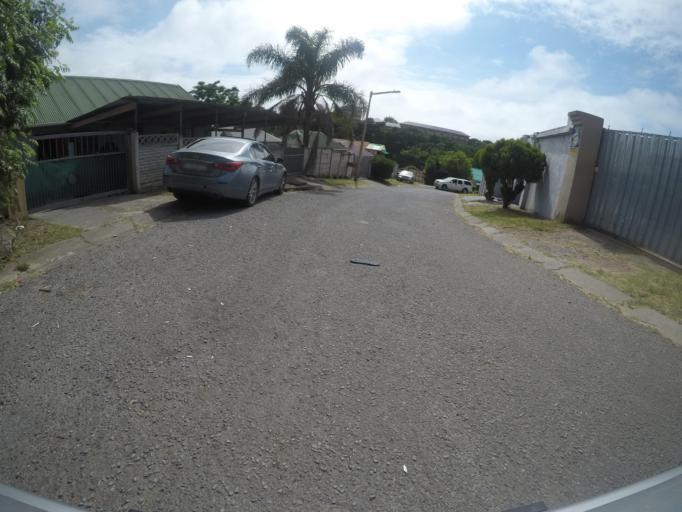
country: ZA
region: Eastern Cape
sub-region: Buffalo City Metropolitan Municipality
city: East London
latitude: -32.9971
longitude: 27.9094
